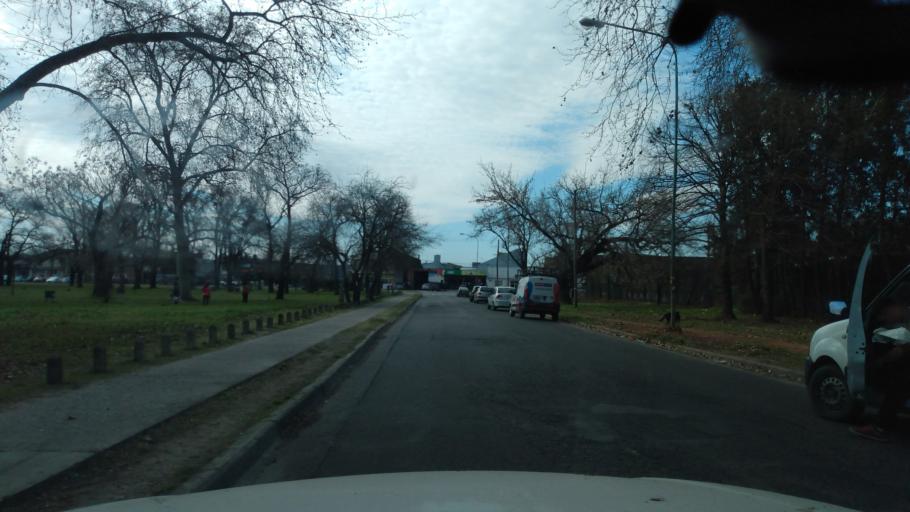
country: AR
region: Buenos Aires
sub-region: Partido de Lujan
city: Lujan
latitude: -34.5604
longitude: -59.1128
